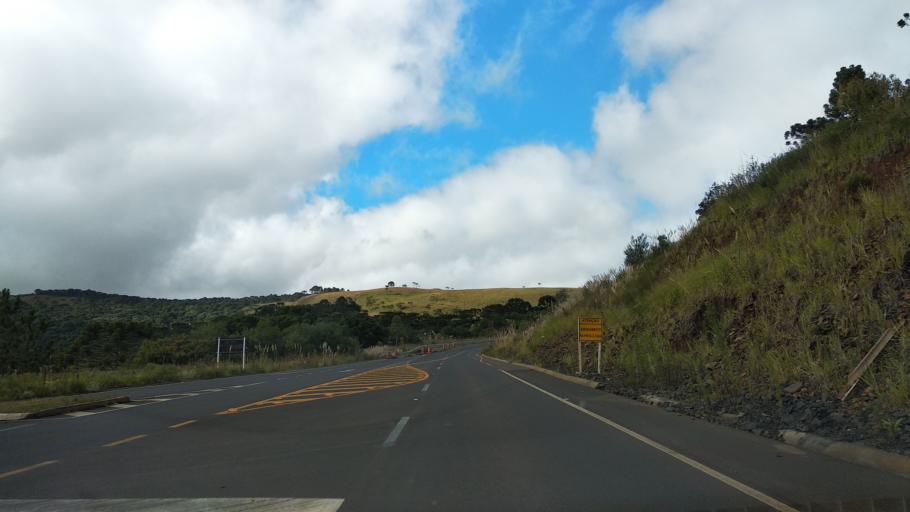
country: BR
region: Santa Catarina
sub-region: Sao Joaquim
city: Sao Joaquim
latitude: -28.2094
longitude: -49.9843
